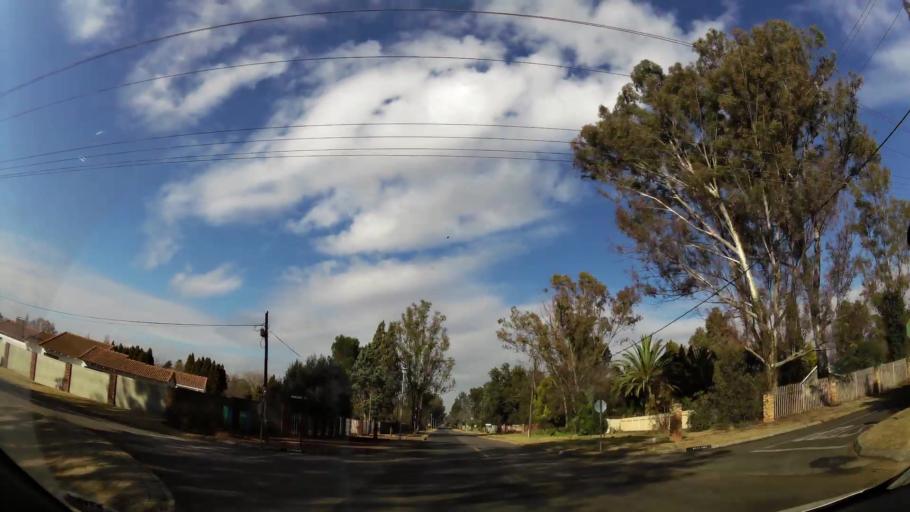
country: ZA
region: Gauteng
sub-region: Sedibeng District Municipality
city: Meyerton
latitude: -26.5342
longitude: 28.0631
